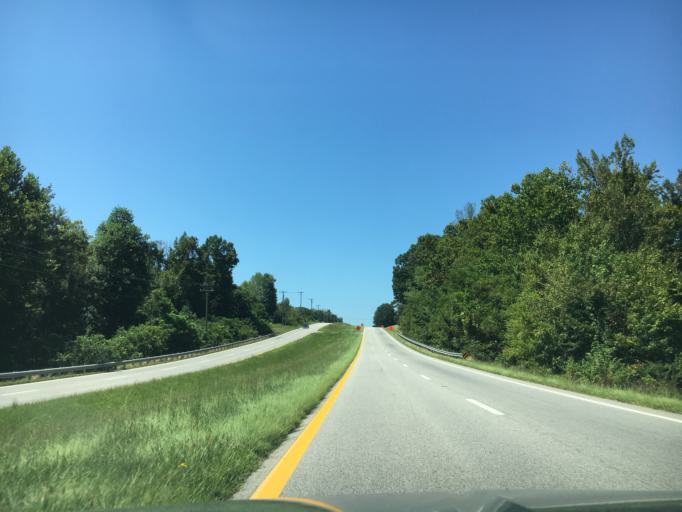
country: US
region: Virginia
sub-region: City of Danville
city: Danville
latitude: 36.5809
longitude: -79.2933
